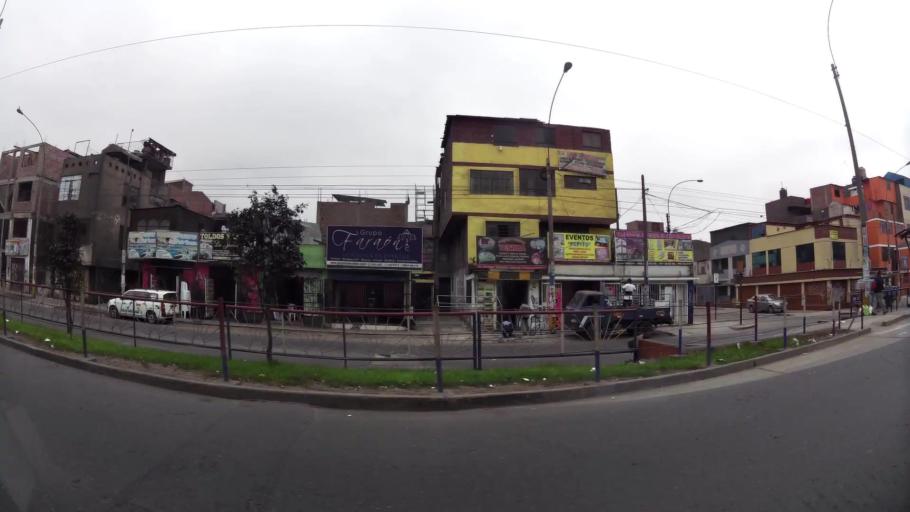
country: PE
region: Lima
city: Lima
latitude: -12.0151
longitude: -77.0017
